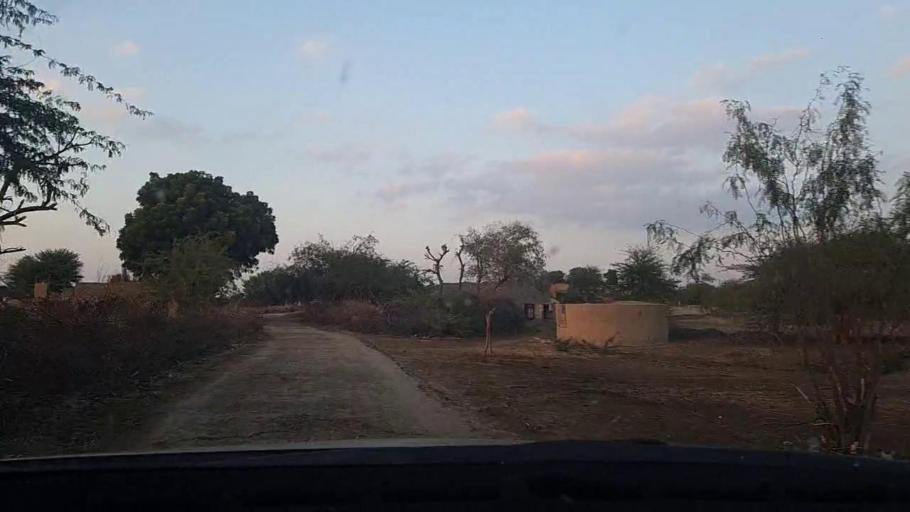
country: PK
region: Sindh
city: Tando Mittha Khan
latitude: 25.9453
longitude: 69.3383
